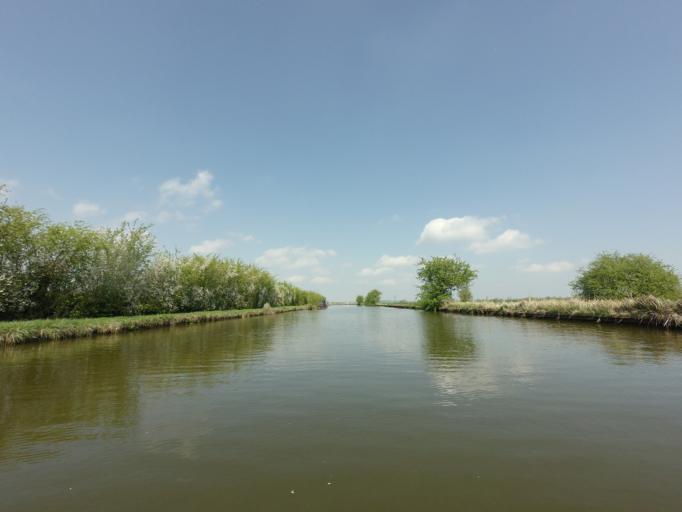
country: GB
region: England
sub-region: Buckinghamshire
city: Ivinghoe
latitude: 51.8505
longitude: -0.6439
